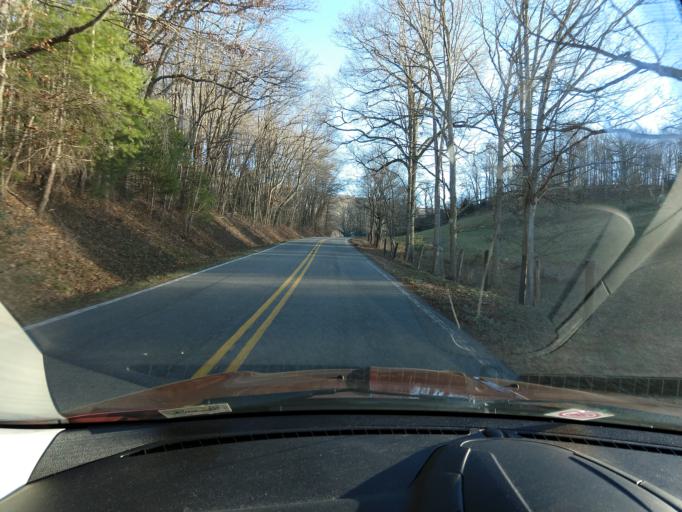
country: US
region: Virginia
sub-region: Alleghany County
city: Clifton Forge
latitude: 37.9043
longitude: -79.8923
